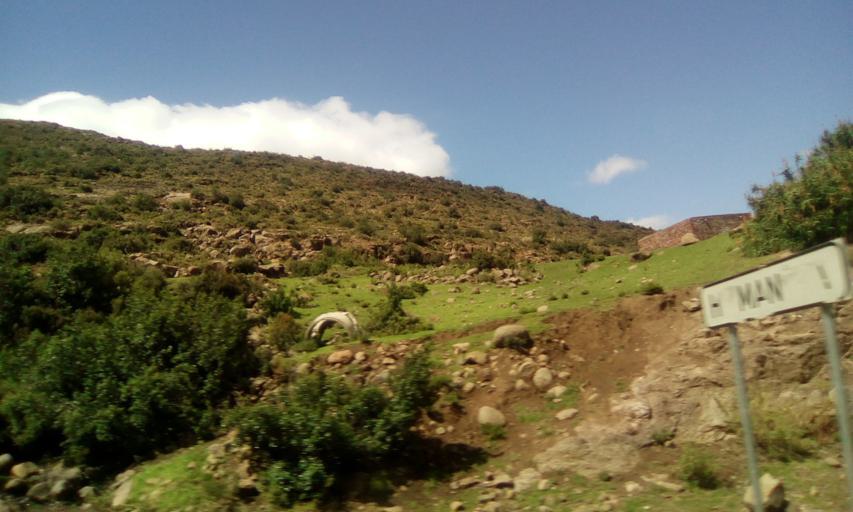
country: LS
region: Maseru
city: Nako
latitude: -29.6562
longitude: 27.8427
